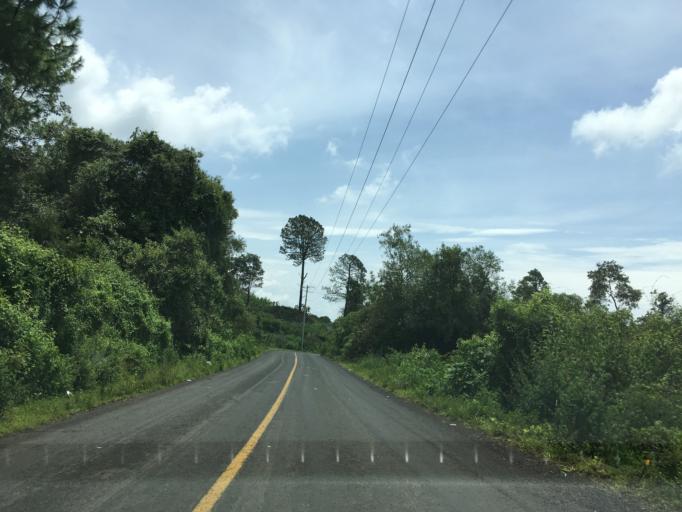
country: MX
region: Michoacan
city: Nuevo San Juan Parangaricutiro
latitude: 19.4286
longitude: -102.1403
